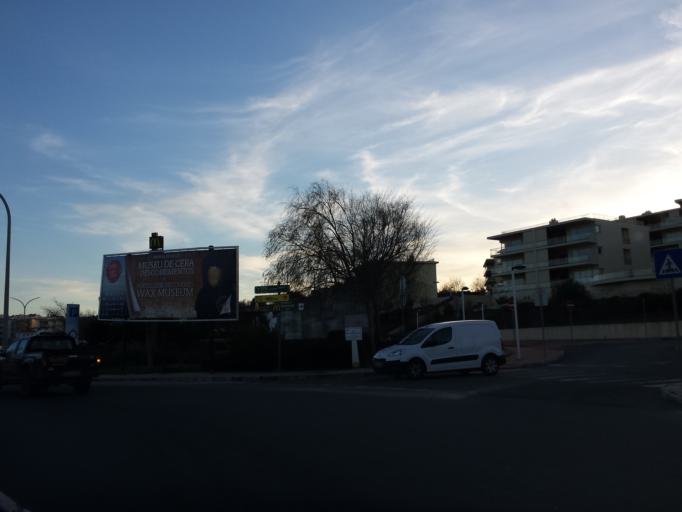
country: PT
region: Faro
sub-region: Lagos
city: Lagos
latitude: 37.1144
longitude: -8.6809
